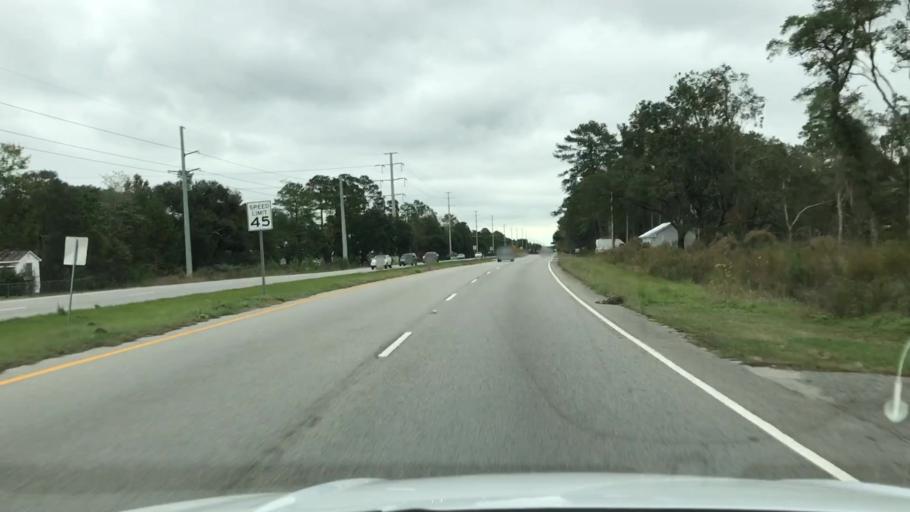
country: US
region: South Carolina
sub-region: Georgetown County
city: Georgetown
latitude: 33.4195
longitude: -79.1779
